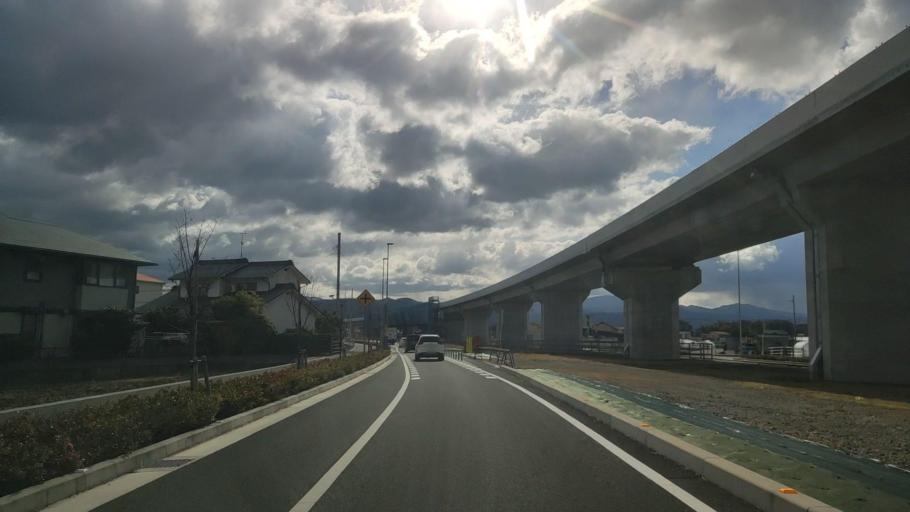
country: JP
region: Ehime
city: Masaki-cho
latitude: 33.8150
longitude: 132.7205
